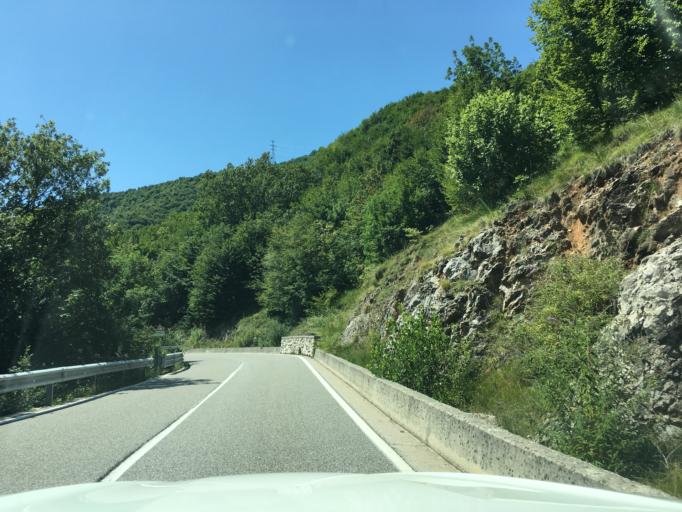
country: IT
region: Lombardy
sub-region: Provincia di Bergamo
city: Selvino
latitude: 45.7693
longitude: 9.7455
